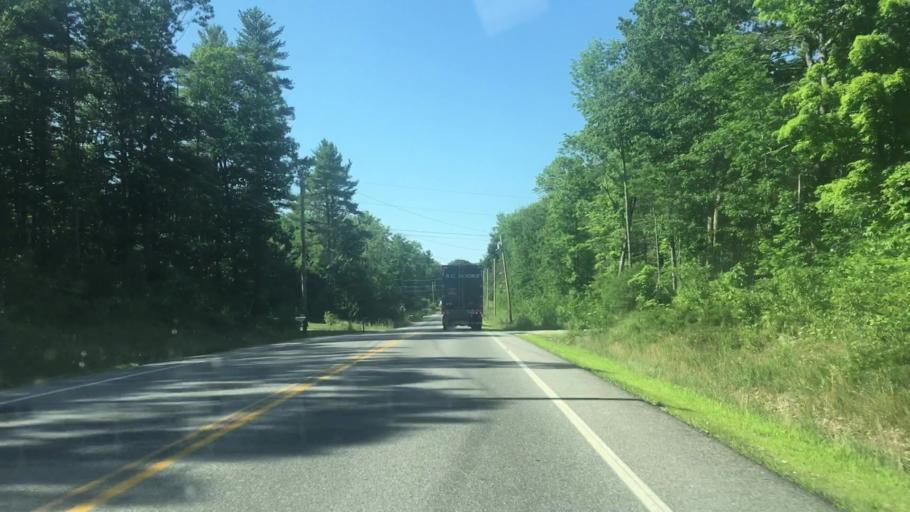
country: US
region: Maine
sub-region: York County
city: Buxton
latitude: 43.5816
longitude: -70.5176
